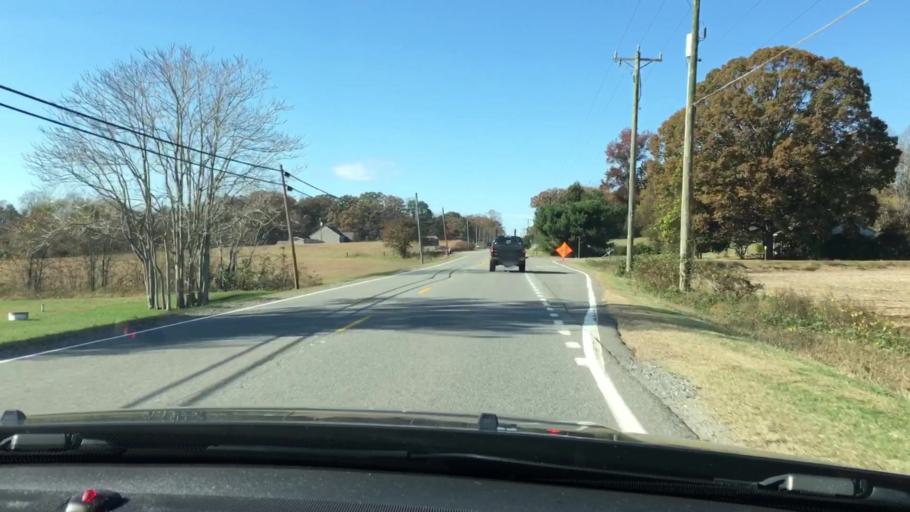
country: US
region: Virginia
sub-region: King William County
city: Central Garage
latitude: 37.7328
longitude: -77.1115
